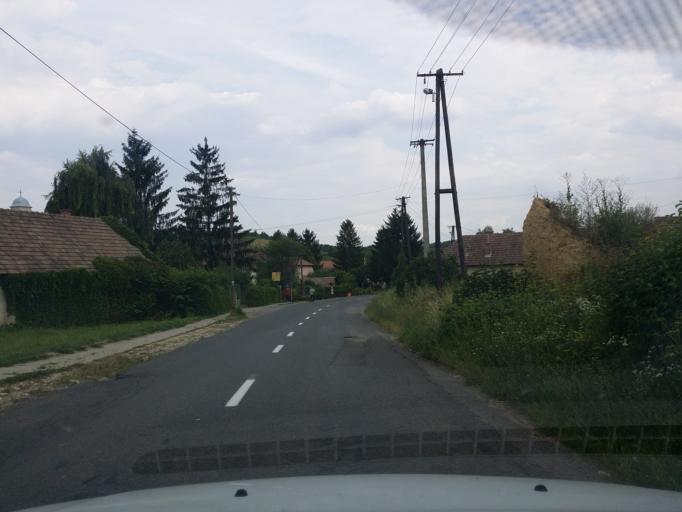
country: HU
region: Nograd
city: Bercel
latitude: 47.9119
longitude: 19.3757
